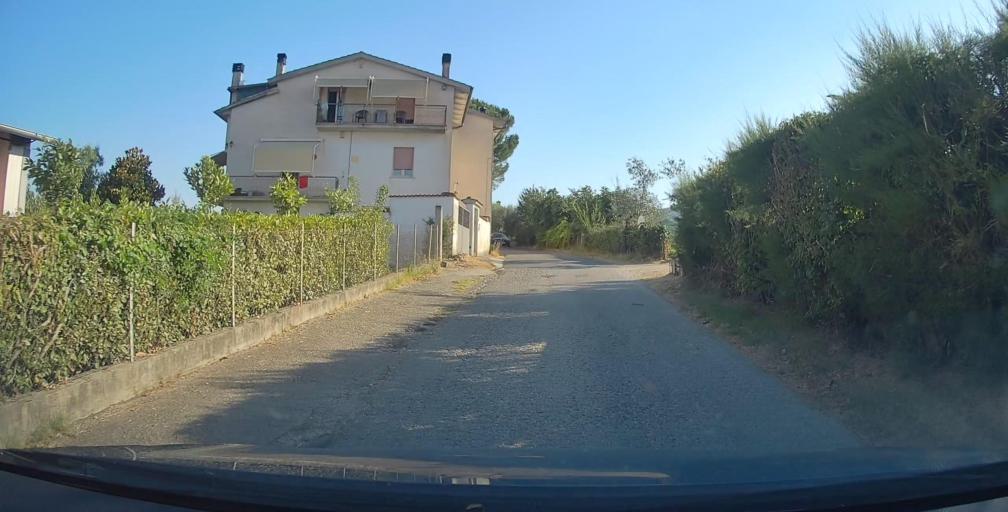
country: IT
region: Umbria
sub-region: Provincia di Terni
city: Calvi dell'Umbria
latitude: 42.3731
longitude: 12.5656
